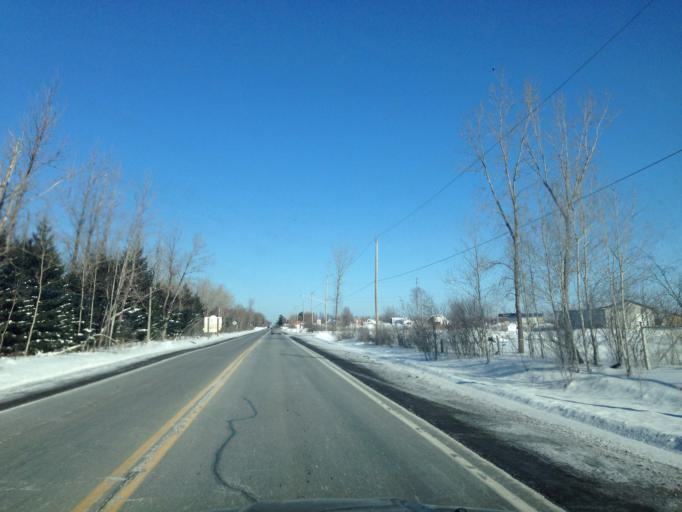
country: CA
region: Ontario
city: Clarence-Rockland
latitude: 45.3354
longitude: -75.4381
